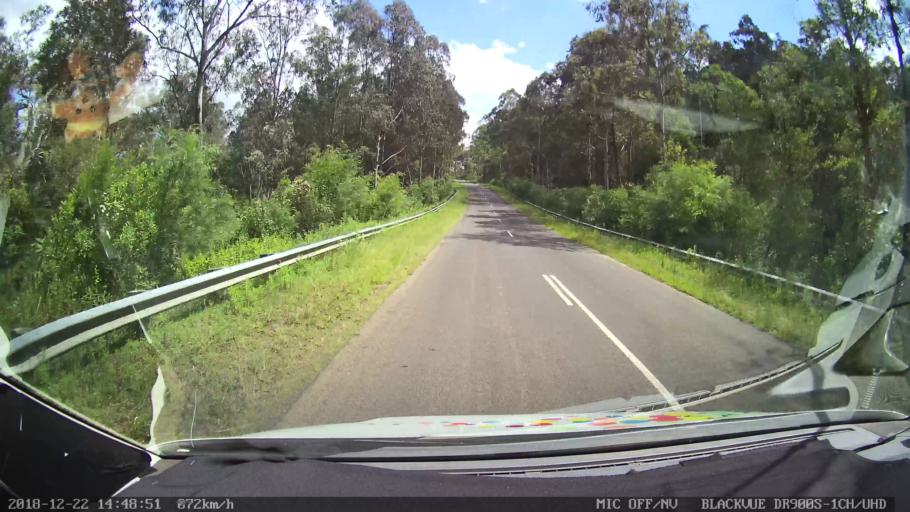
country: AU
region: New South Wales
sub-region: Bellingen
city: Dorrigo
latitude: -30.1843
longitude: 152.5514
